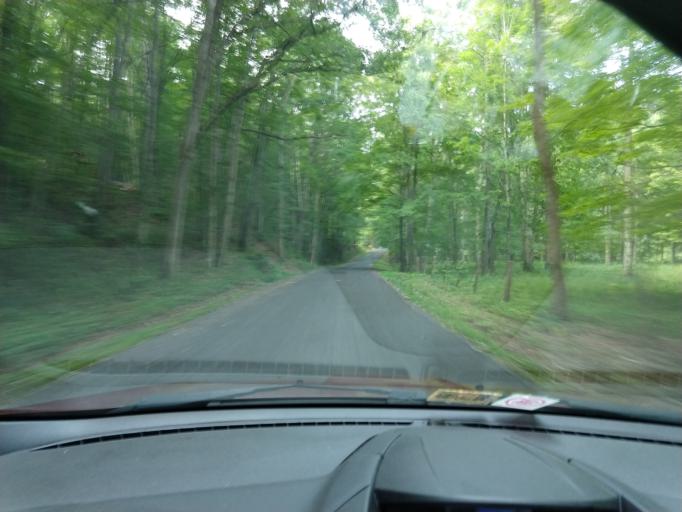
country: US
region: Virginia
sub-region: City of Covington
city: Covington
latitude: 37.8956
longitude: -80.0876
